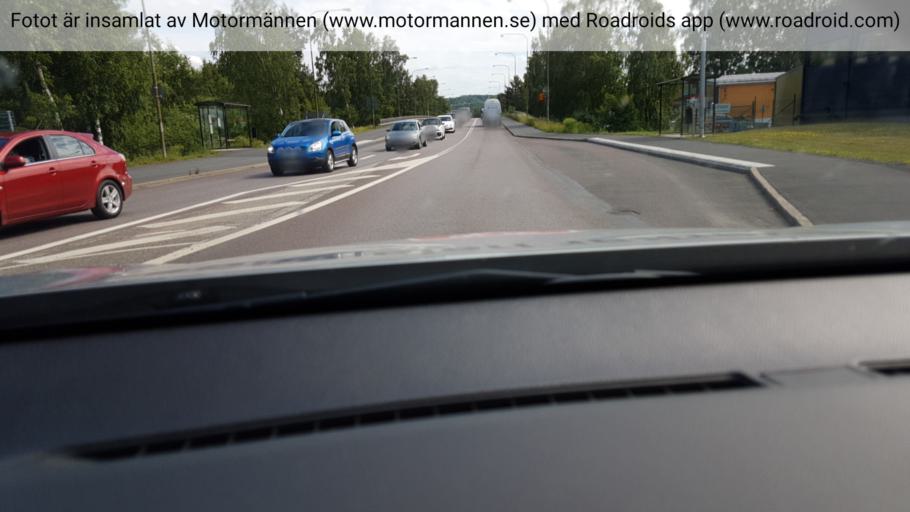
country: SE
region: Joenkoeping
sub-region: Jonkopings Kommun
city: Jonkoping
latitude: 57.7612
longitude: 14.1675
